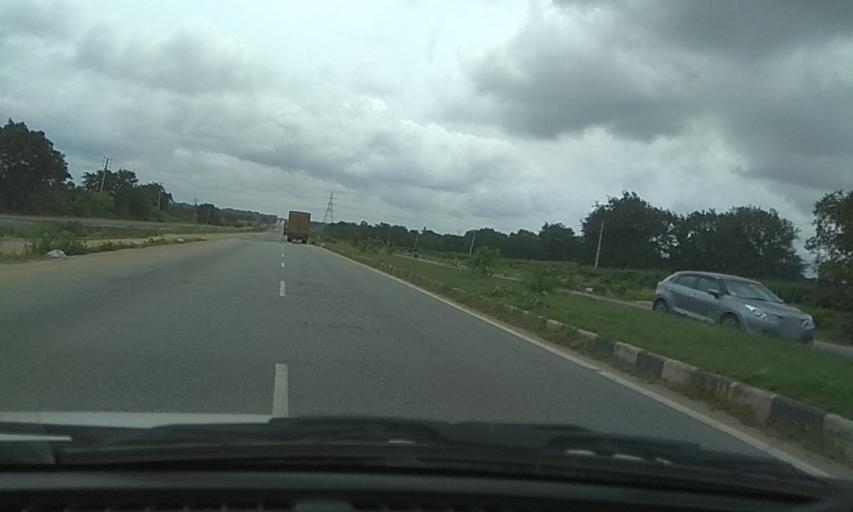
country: IN
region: Karnataka
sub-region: Davanagere
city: Mayakonda
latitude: 14.3706
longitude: 76.1293
